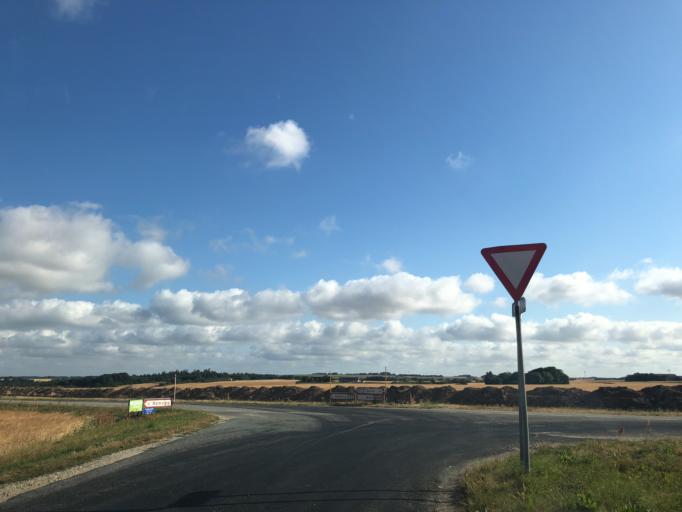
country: DK
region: Central Jutland
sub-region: Holstebro Kommune
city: Vinderup
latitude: 56.6275
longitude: 8.8466
